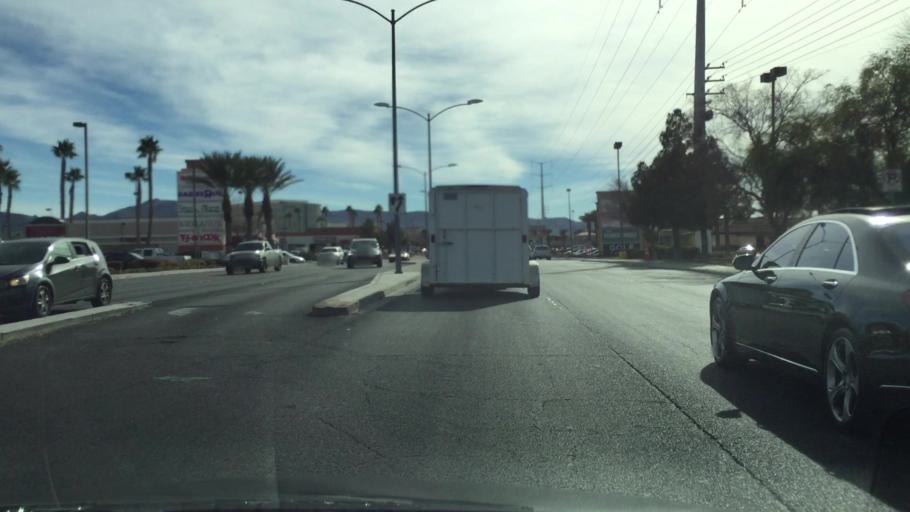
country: US
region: Nevada
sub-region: Clark County
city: Whitney
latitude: 36.0622
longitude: -115.0463
